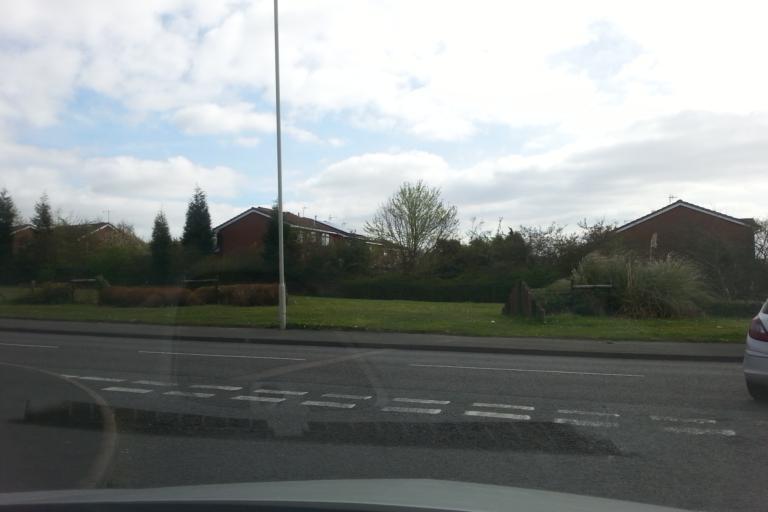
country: GB
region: England
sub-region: Dudley
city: Brierley Hill
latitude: 52.5167
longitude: -2.1183
